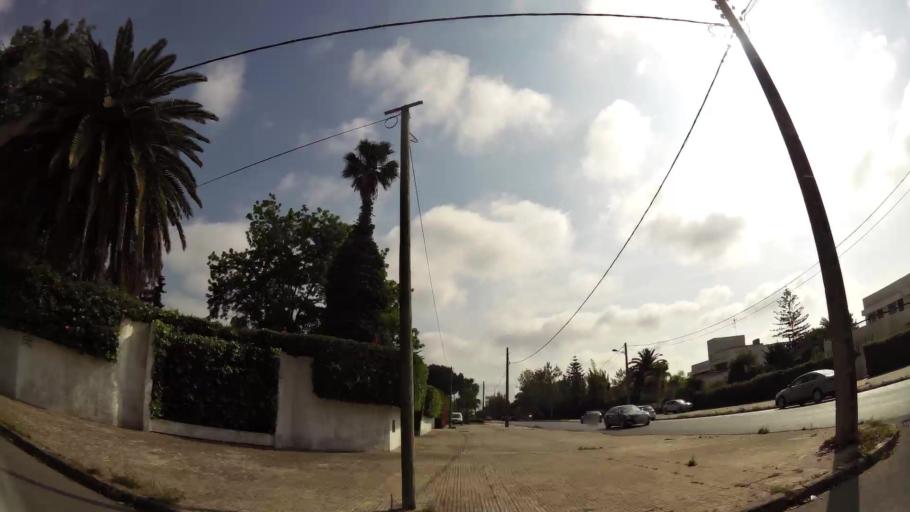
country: MA
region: Rabat-Sale-Zemmour-Zaer
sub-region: Rabat
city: Rabat
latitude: 33.9696
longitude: -6.8583
